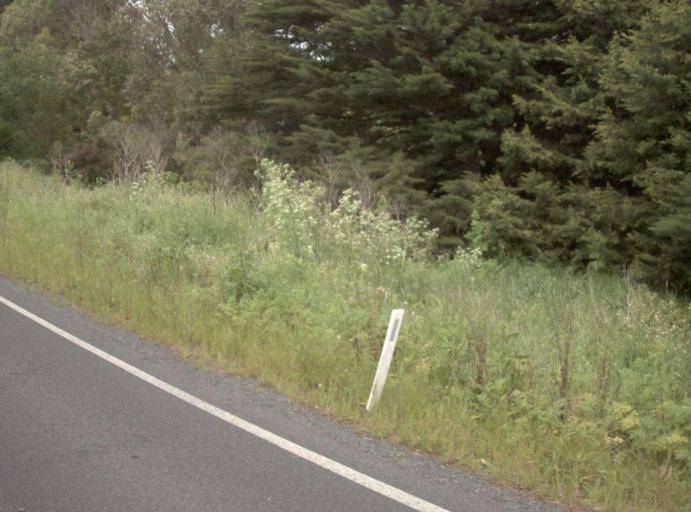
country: AU
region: Victoria
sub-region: Bass Coast
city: North Wonthaggi
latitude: -38.4892
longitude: 145.7482
